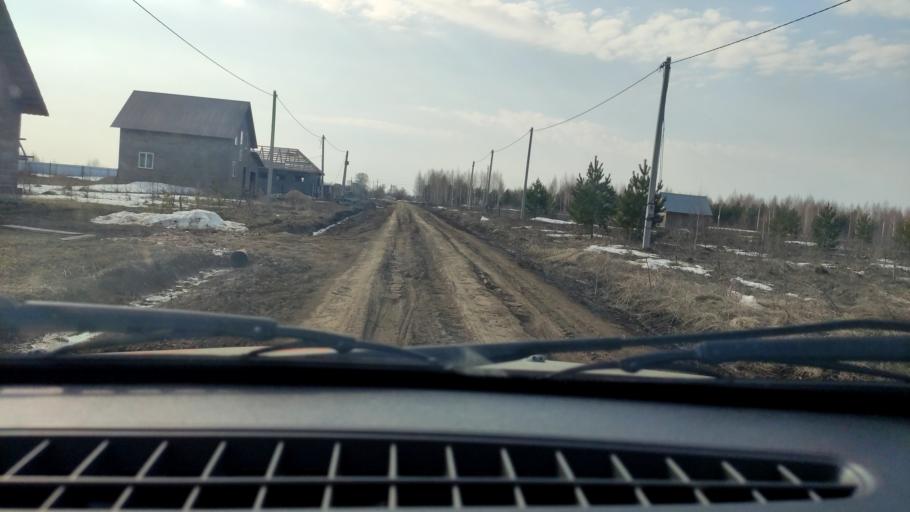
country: RU
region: Bashkortostan
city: Iglino
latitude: 54.7917
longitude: 56.4041
